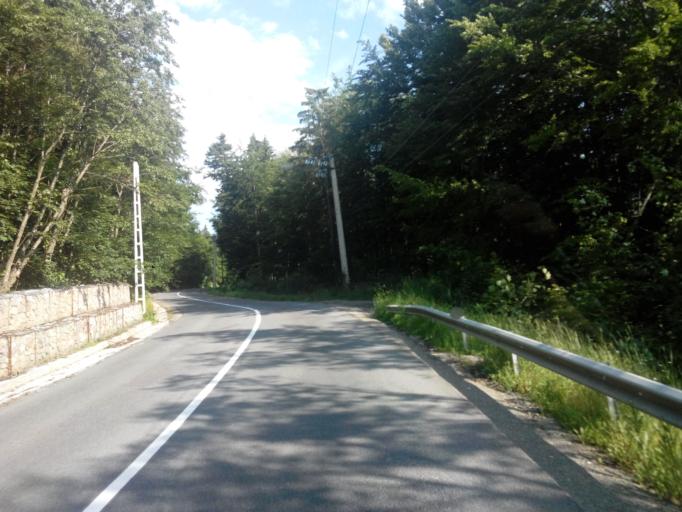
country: RO
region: Brasov
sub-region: Oras Predeal
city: Predeal
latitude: 45.4990
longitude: 25.5162
